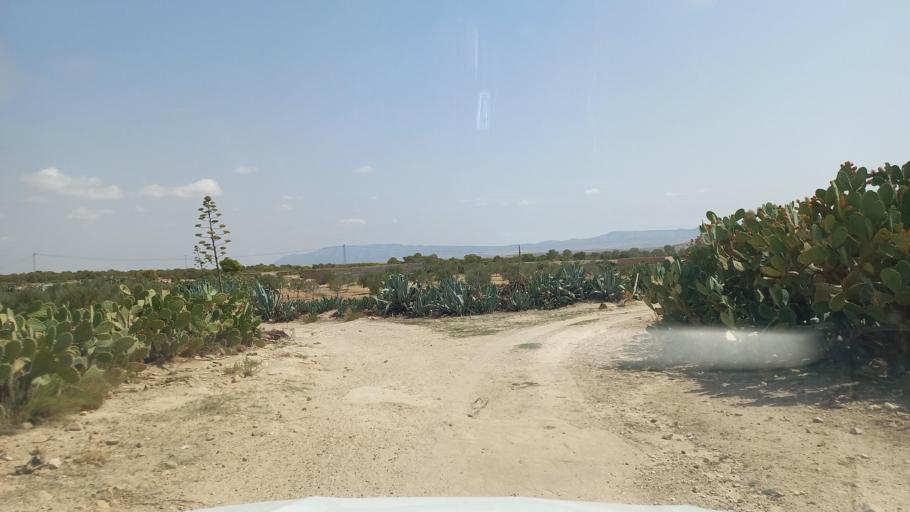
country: TN
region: Al Qasrayn
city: Sbiba
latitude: 35.3985
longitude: 8.9818
